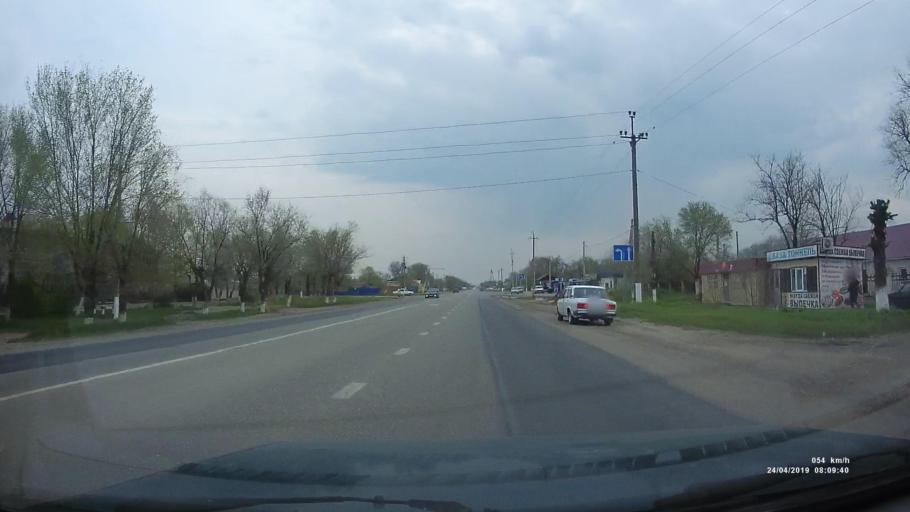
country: RU
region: Kalmykiya
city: Priyutnoye
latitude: 46.0965
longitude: 43.5079
